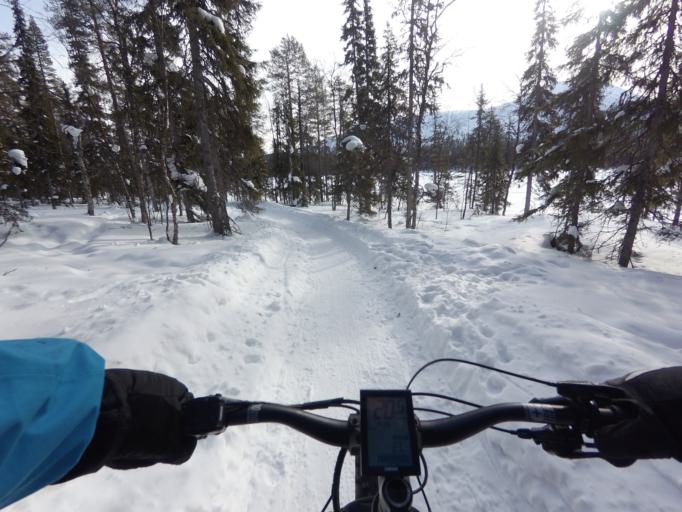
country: FI
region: Lapland
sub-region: Tunturi-Lappi
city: Kolari
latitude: 67.6013
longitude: 24.2391
